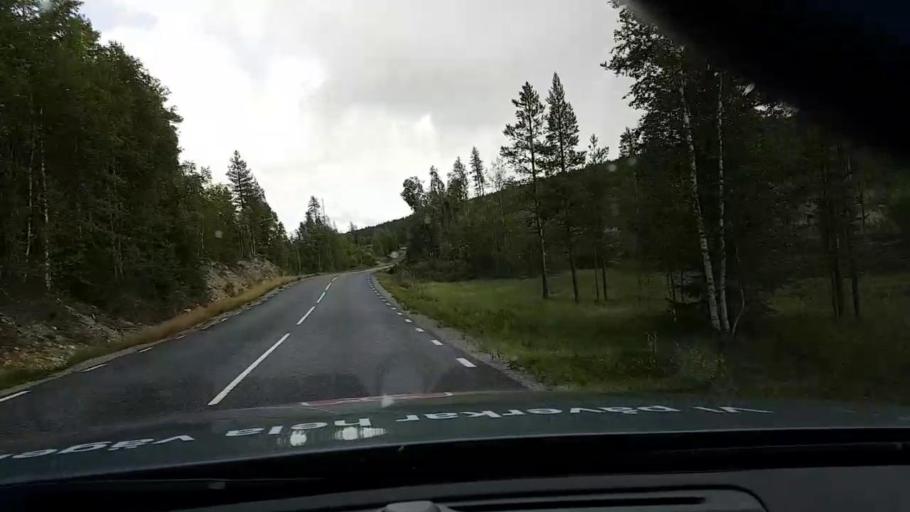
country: SE
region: Vaesterbotten
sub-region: Asele Kommun
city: Asele
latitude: 63.8329
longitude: 17.4498
